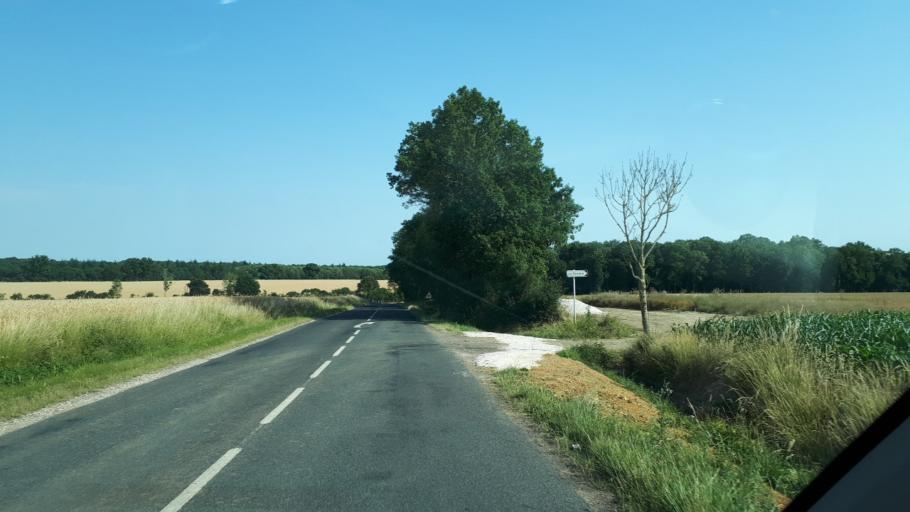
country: FR
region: Centre
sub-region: Departement du Loir-et-Cher
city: La Ville-aux-Clercs
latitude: 47.9403
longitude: 1.0820
